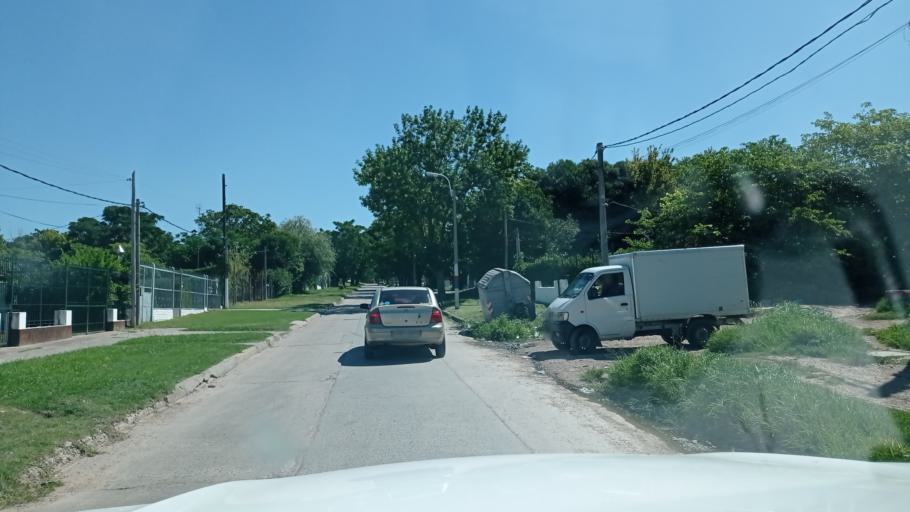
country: UY
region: Montevideo
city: Montevideo
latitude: -34.8655
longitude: -56.2603
